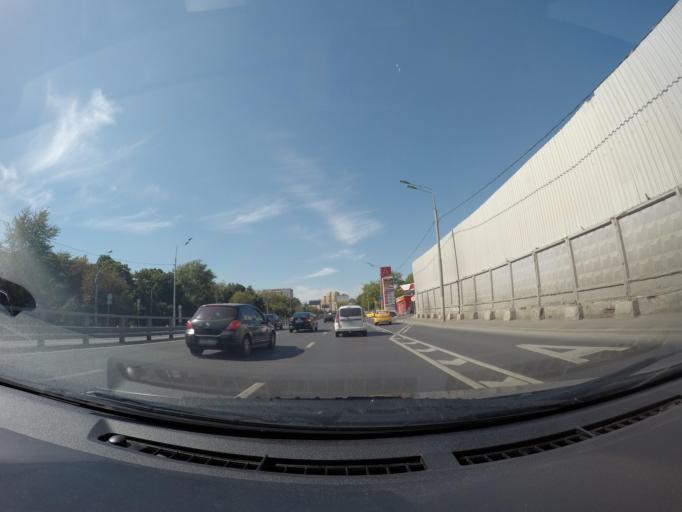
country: RU
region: Moscow
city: Lefortovo
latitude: 55.7344
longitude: 37.7085
